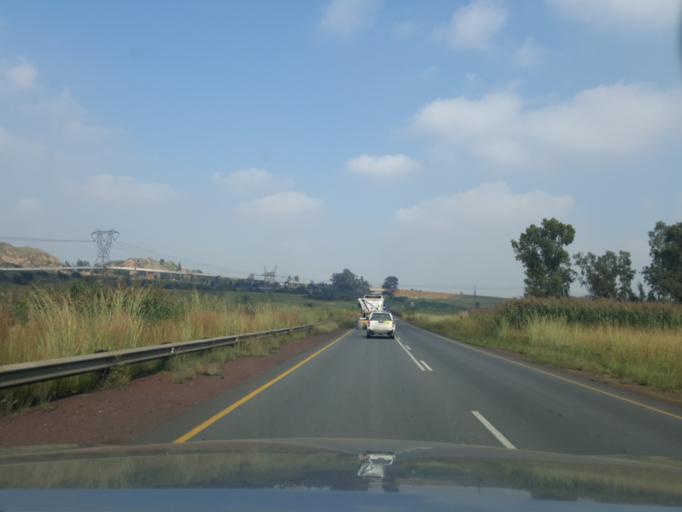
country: ZA
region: Mpumalanga
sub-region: Nkangala District Municipality
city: Witbank
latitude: -26.0140
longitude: 29.3693
